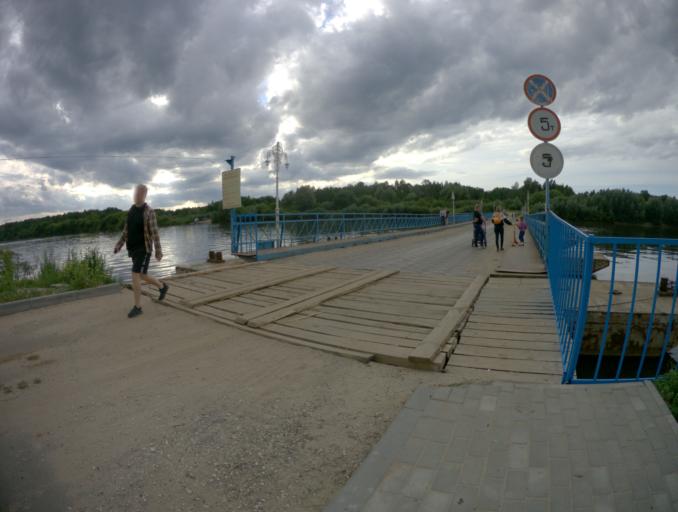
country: RU
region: Vladimir
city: Gorokhovets
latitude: 56.2088
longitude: 42.6794
